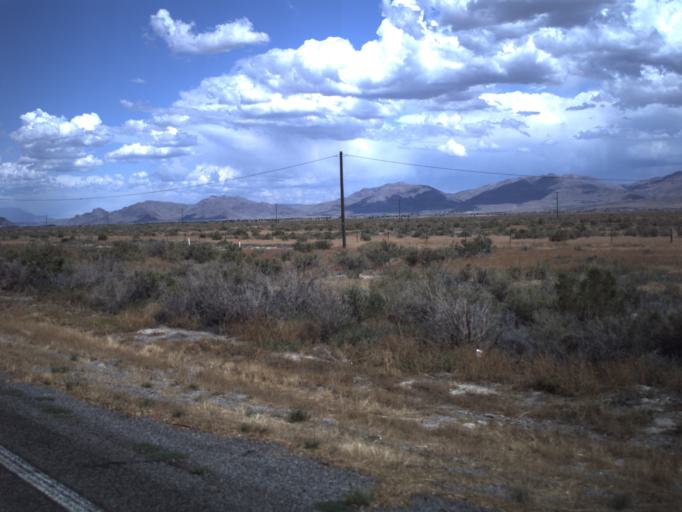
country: US
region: Utah
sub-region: Millard County
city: Delta
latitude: 39.4604
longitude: -112.4346
